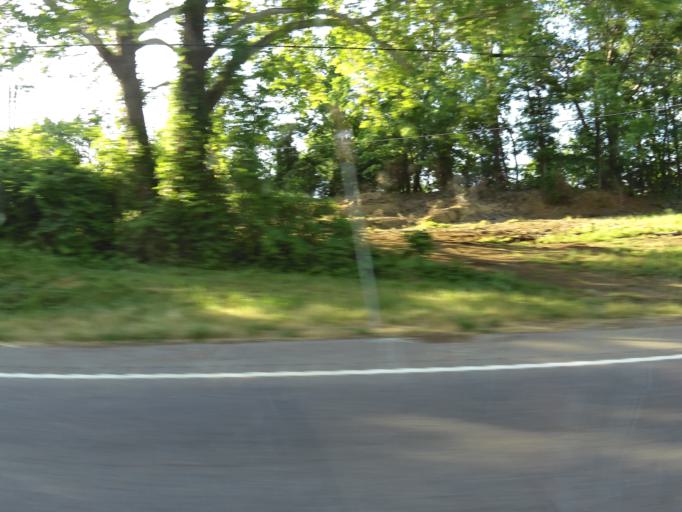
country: US
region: Tennessee
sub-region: Sevier County
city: Seymour
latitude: 35.8659
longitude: -83.6610
